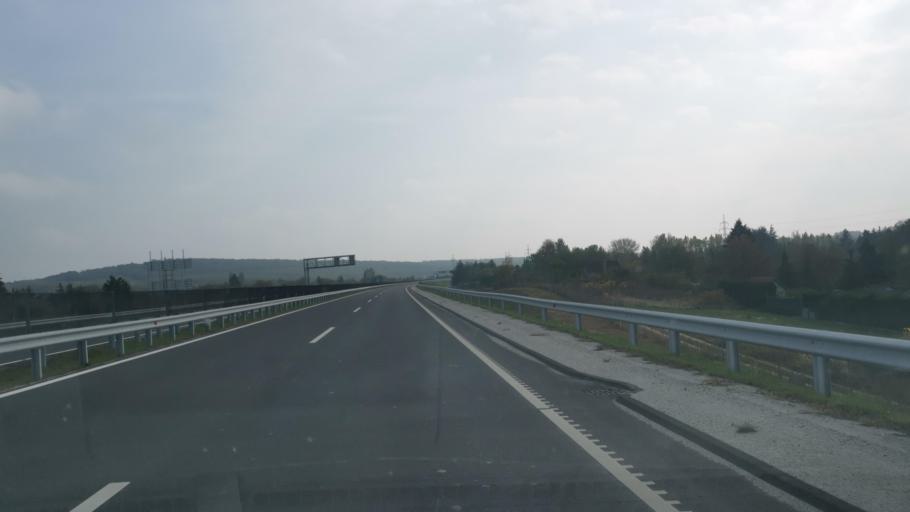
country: HU
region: Gyor-Moson-Sopron
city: Sopron
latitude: 47.6992
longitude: 16.6155
